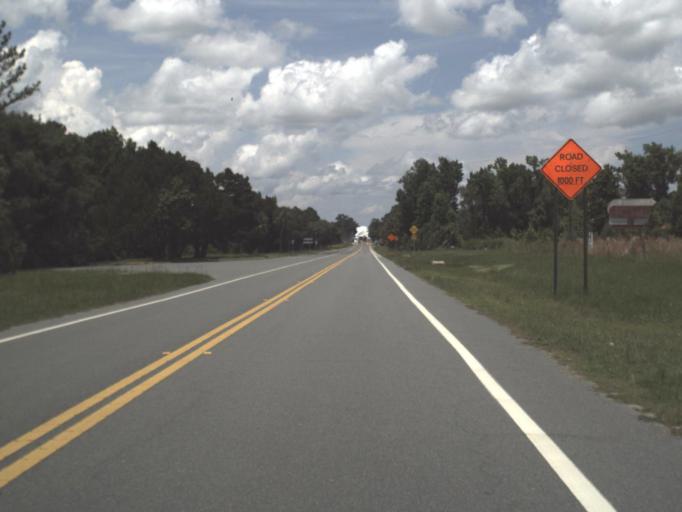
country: US
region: Georgia
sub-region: Camden County
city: Kingsland
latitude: 30.7351
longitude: -81.6882
